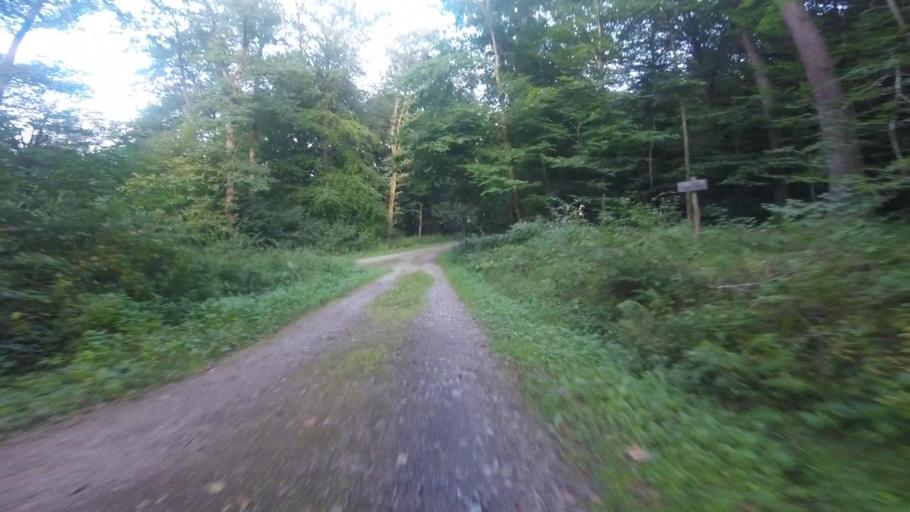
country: DE
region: Baden-Wuerttemberg
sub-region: Regierungsbezirk Stuttgart
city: Aspach
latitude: 48.9723
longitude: 9.3691
